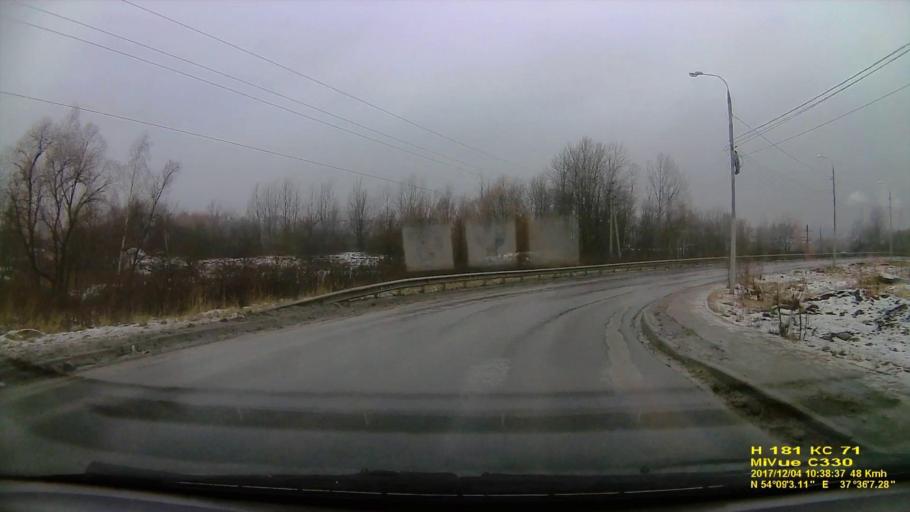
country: RU
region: Tula
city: Mendeleyevskiy
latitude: 54.1512
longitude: 37.6022
